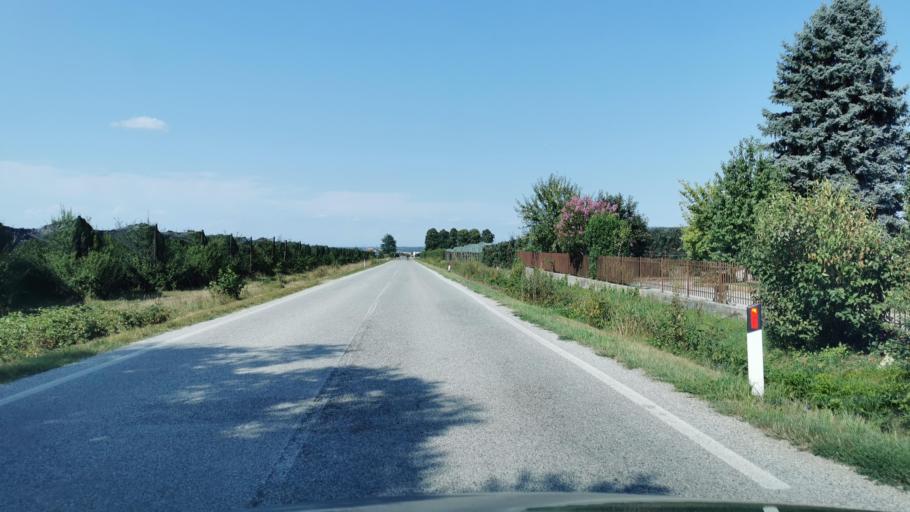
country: IT
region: Piedmont
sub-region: Provincia di Cuneo
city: Revello
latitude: 44.6650
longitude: 7.3957
